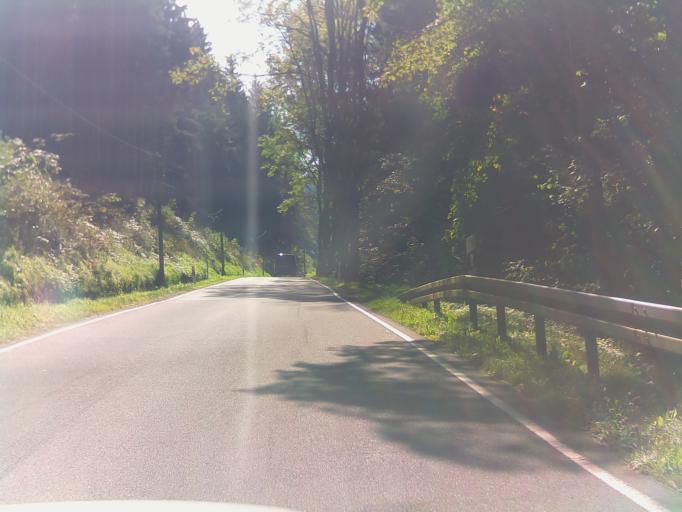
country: DE
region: Thuringia
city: Leutenberg
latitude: 50.5187
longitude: 11.4831
